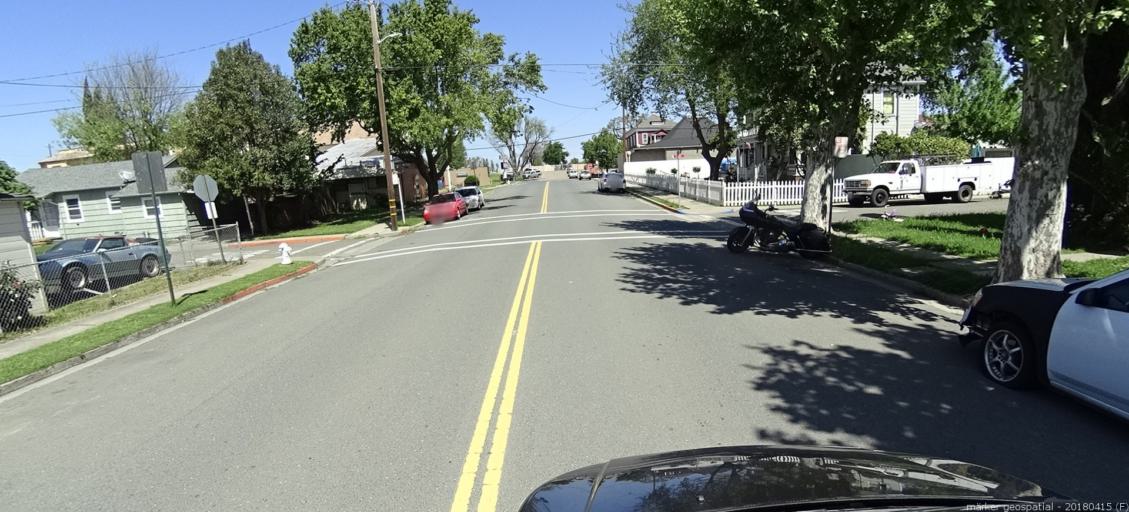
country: US
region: California
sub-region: Solano County
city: Rio Vista
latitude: 38.1608
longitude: -121.6114
